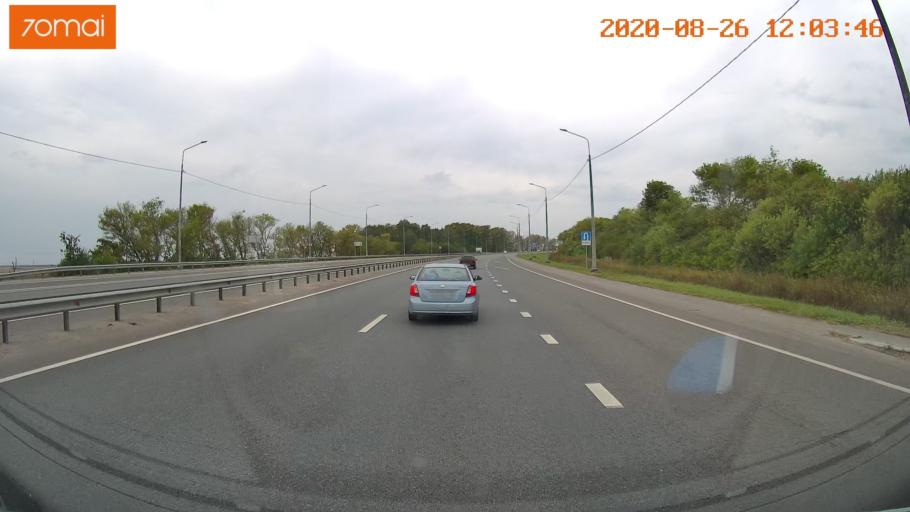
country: RU
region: Rjazan
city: Kiritsy
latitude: 54.3032
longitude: 40.1997
